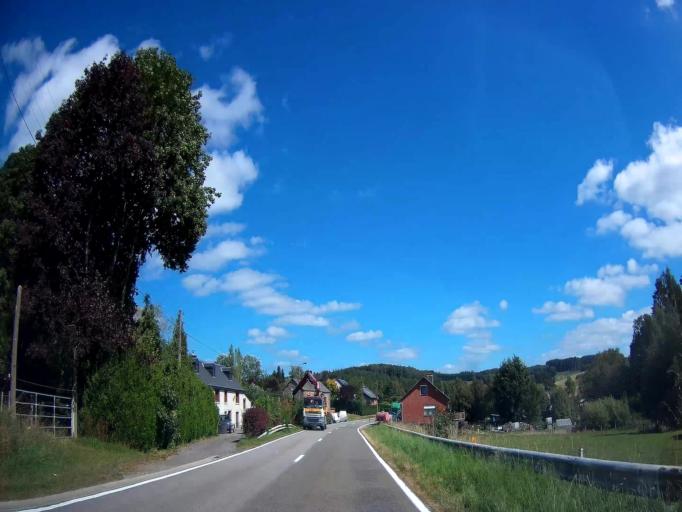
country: BE
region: Wallonia
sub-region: Province du Luxembourg
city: Bertogne
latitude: 50.0893
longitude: 5.6715
